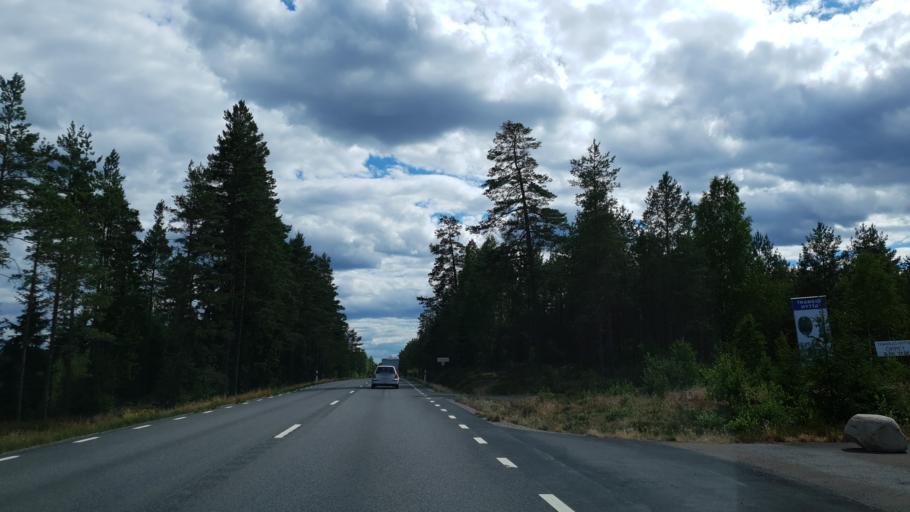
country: SE
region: Kronoberg
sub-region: Lessebo Kommun
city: Lessebo
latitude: 56.8024
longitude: 15.4124
